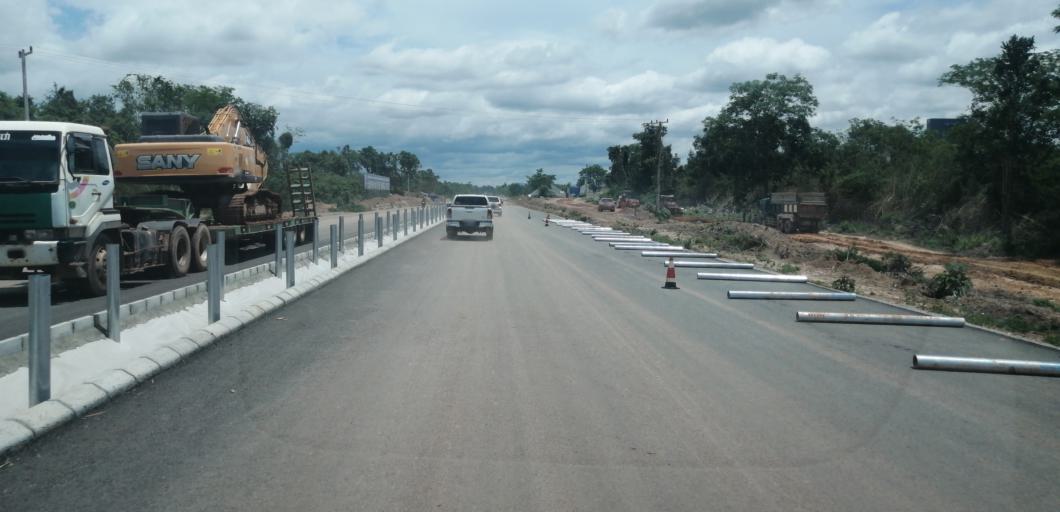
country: LA
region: Vientiane
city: Muang Phon-Hong
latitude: 18.2954
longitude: 102.4570
